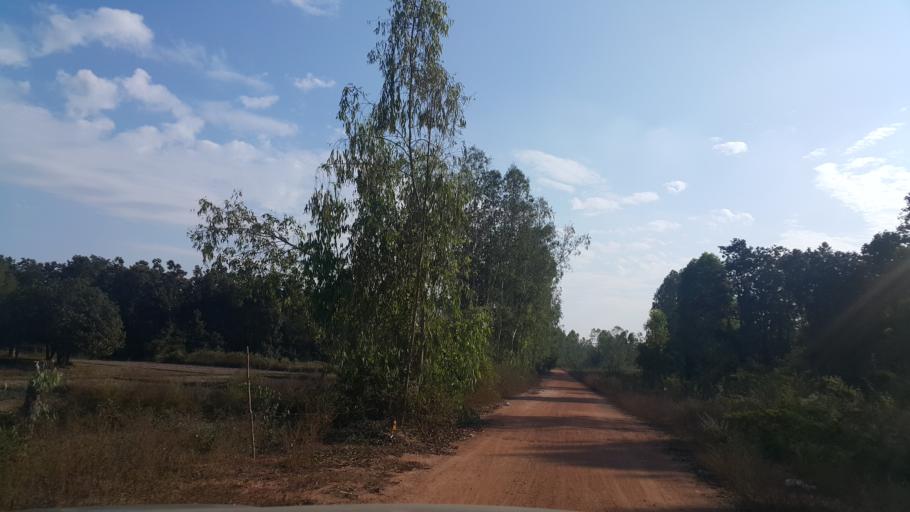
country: TH
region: Lampang
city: Hang Chat
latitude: 18.2664
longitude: 99.3719
